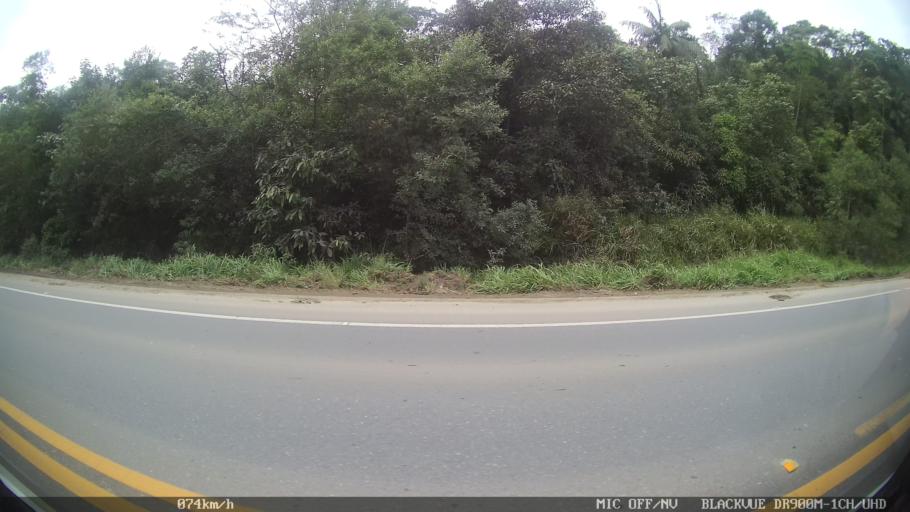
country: BR
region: Santa Catarina
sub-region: Joinville
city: Joinville
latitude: -26.2635
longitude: -48.9169
